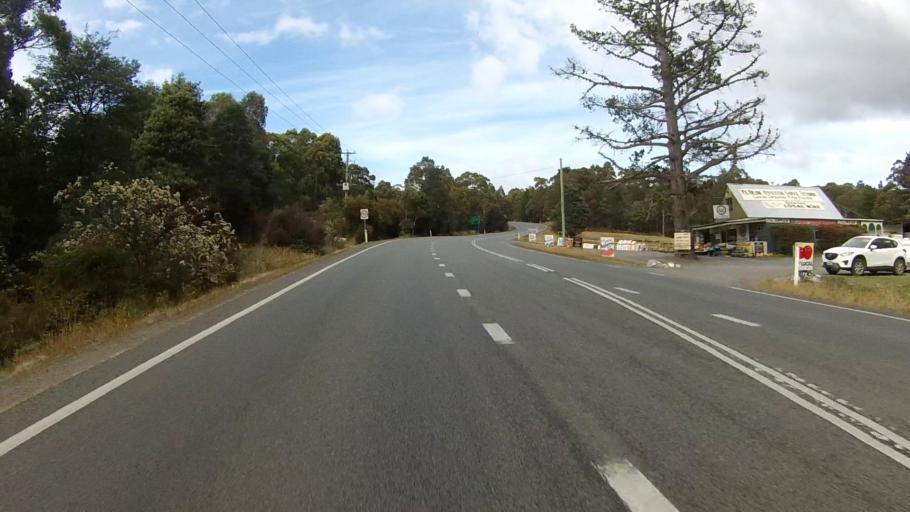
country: AU
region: Tasmania
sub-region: Kingborough
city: Kettering
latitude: -43.1068
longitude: 147.2445
